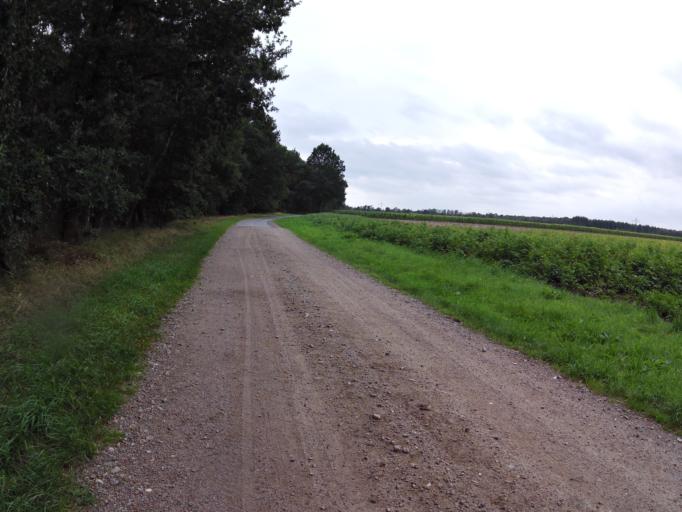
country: DE
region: Lower Saxony
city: Scheessel
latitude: 53.1474
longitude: 9.4479
